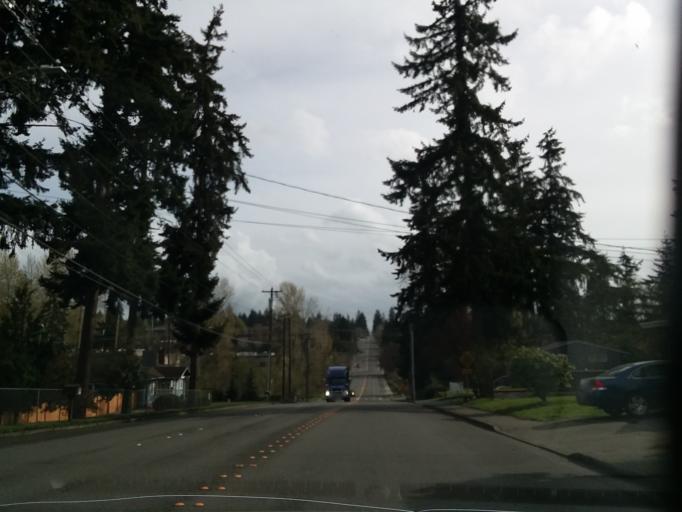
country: US
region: Washington
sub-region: Snohomish County
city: Lynnwood
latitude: 47.8059
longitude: -122.3220
